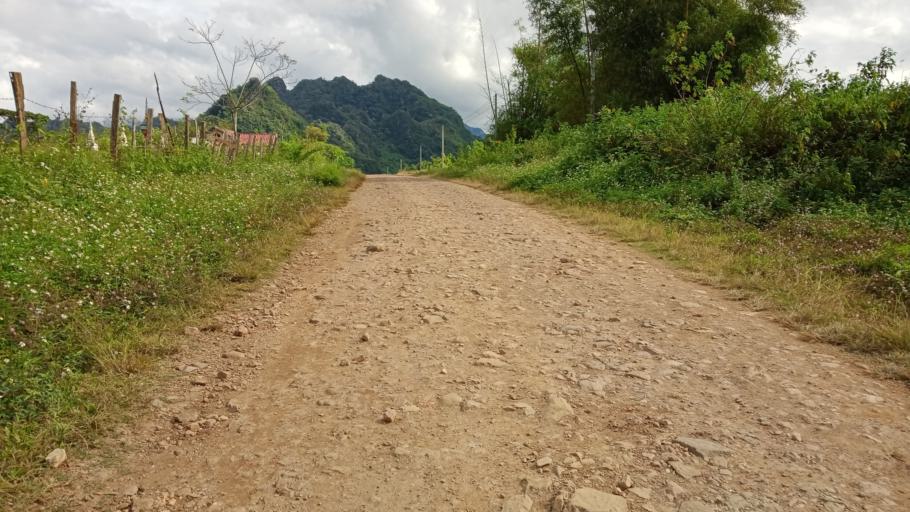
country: LA
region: Xiangkhoang
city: Phonsavan
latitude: 19.1059
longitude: 102.9298
